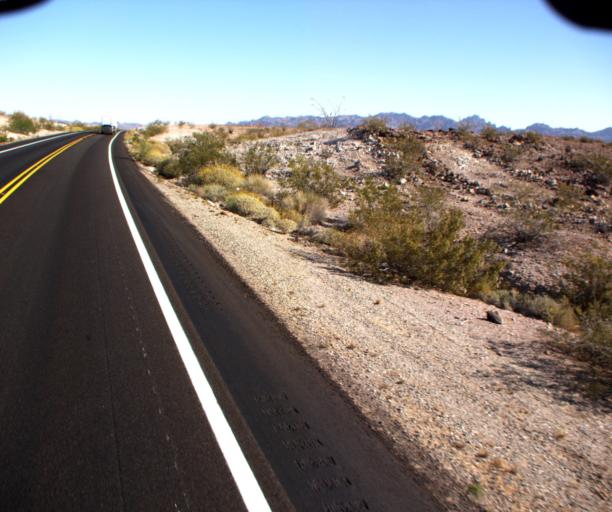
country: US
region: Arizona
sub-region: Yuma County
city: Wellton
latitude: 33.1017
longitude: -114.2979
